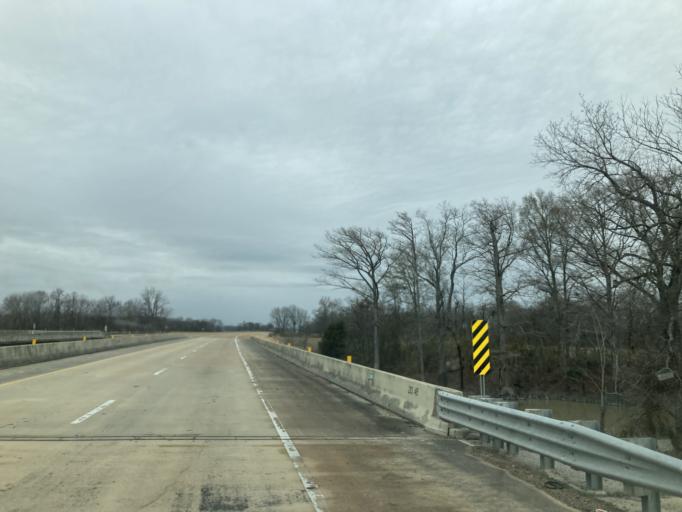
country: US
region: Mississippi
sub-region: Yazoo County
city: Yazoo City
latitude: 32.9984
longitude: -90.4698
